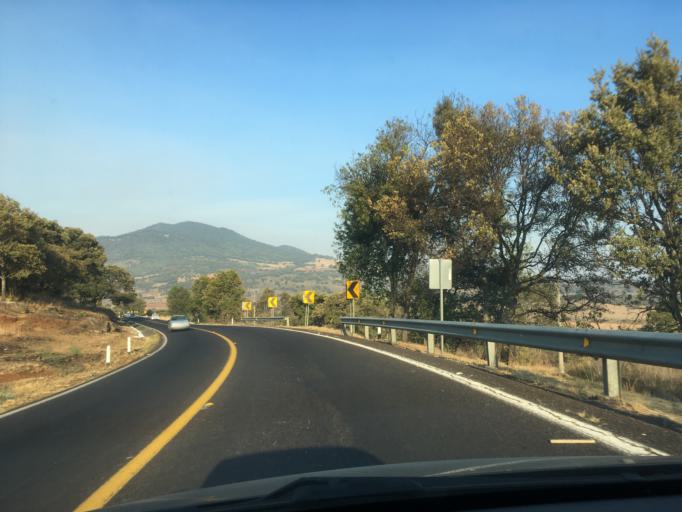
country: MX
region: Michoacan
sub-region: Morelia
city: Iratzio
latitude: 19.6280
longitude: -101.4343
